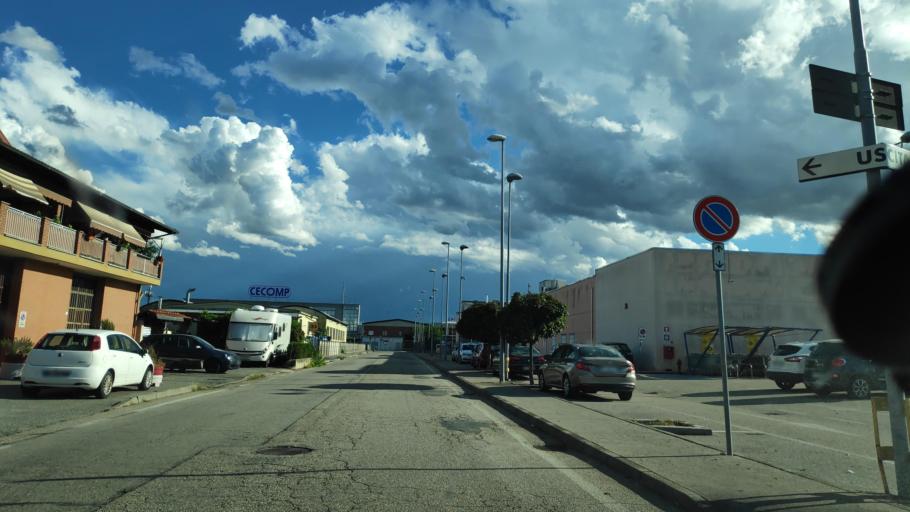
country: IT
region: Piedmont
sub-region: Provincia di Torino
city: La Loggia
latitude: 44.9642
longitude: 7.6695
